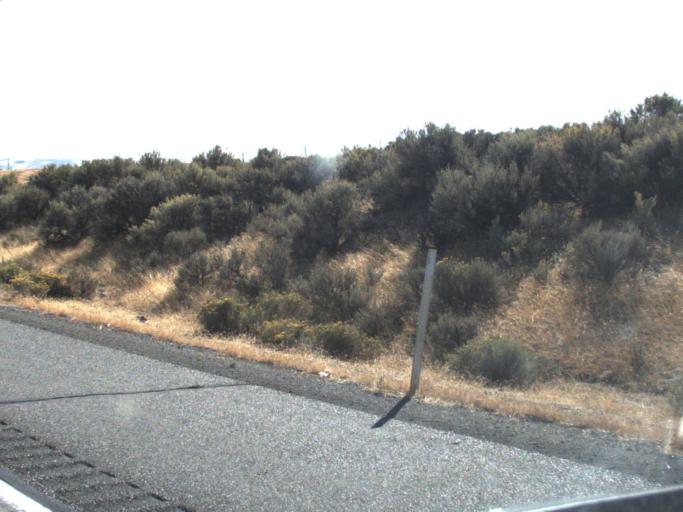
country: US
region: Washington
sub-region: Benton County
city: West Richland
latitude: 46.2272
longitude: -119.3538
